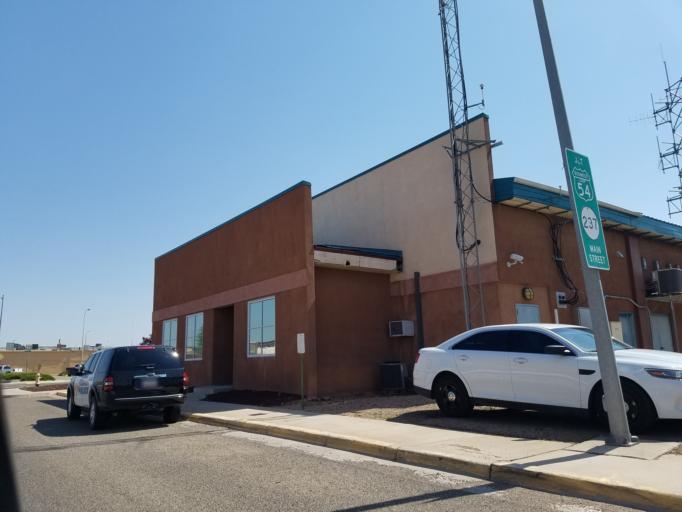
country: US
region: New Mexico
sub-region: Quay County
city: Tucumcari
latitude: 35.1773
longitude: -103.7248
